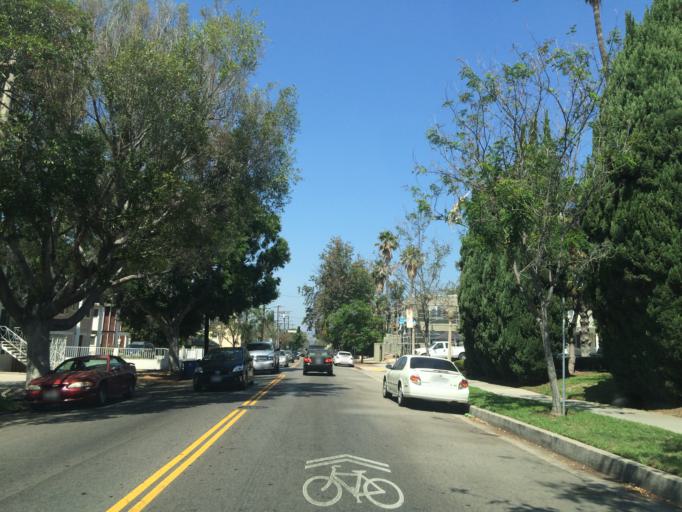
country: US
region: California
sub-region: Los Angeles County
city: Silver Lake
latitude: 34.1054
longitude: -118.2945
